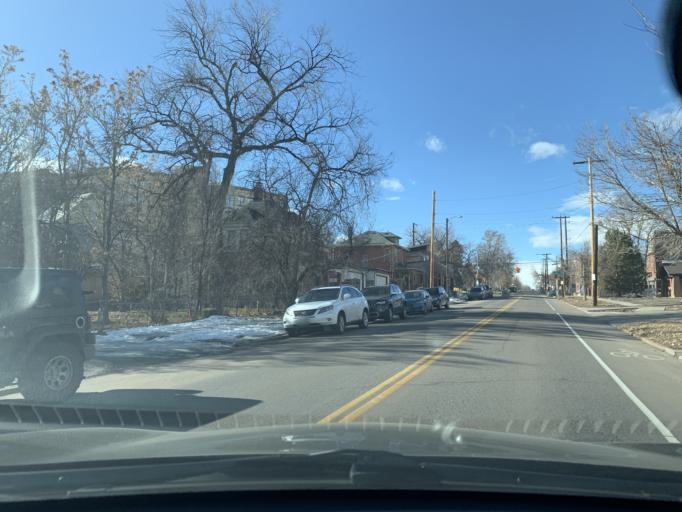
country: US
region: Colorado
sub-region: Denver County
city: Denver
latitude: 39.7513
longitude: -105.0192
